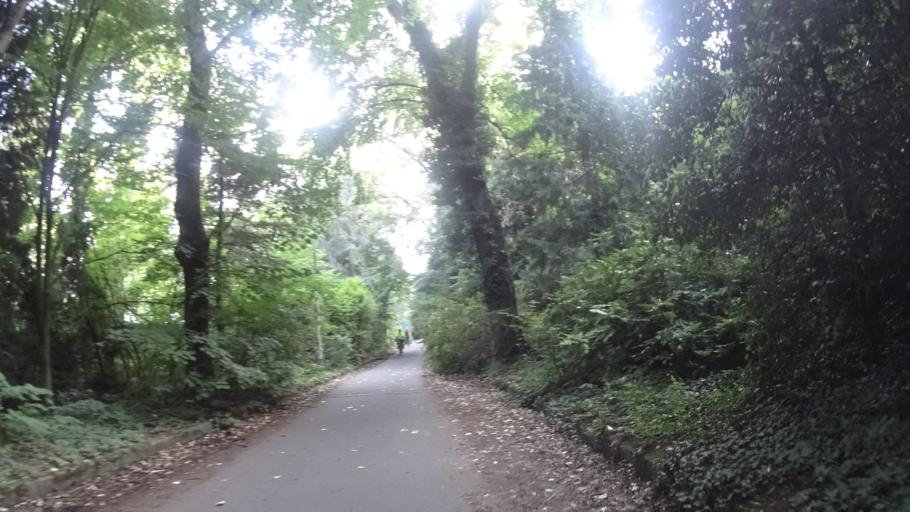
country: HU
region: Fejer
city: Lepseny
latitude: 46.9916
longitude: 18.1683
